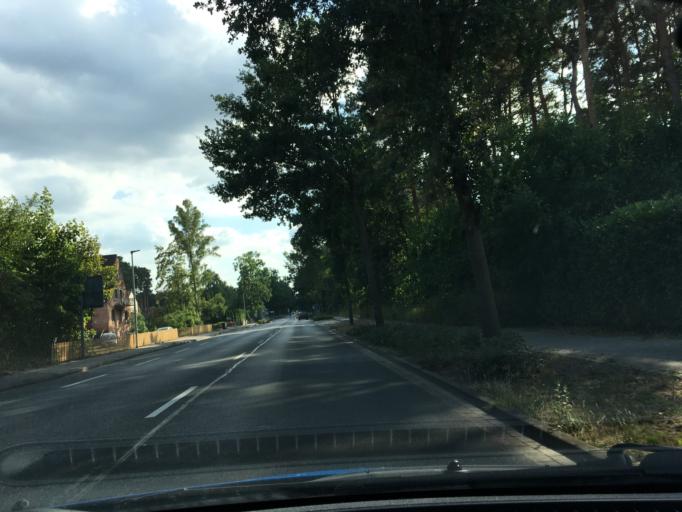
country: DE
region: Lower Saxony
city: Dannenberg
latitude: 53.0860
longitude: 11.0818
